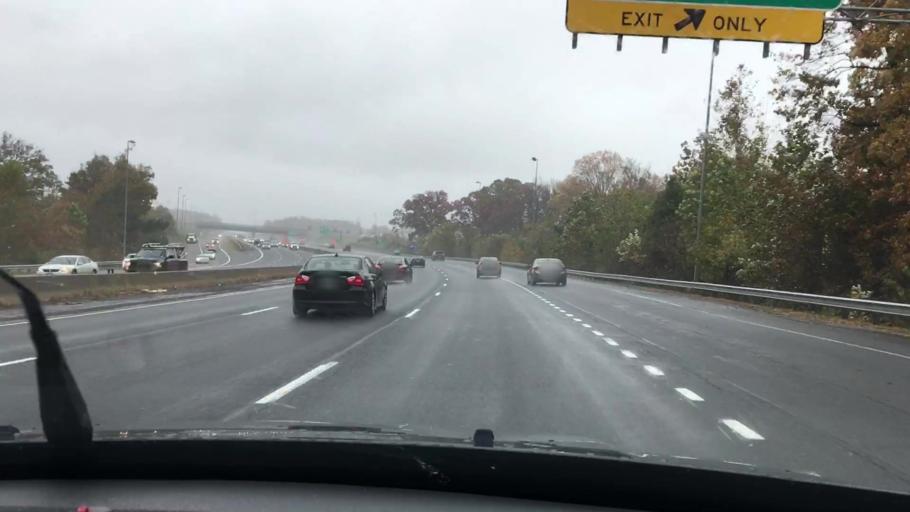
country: US
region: Virginia
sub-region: Fairfax County
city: Chantilly
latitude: 38.8791
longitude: -77.4493
